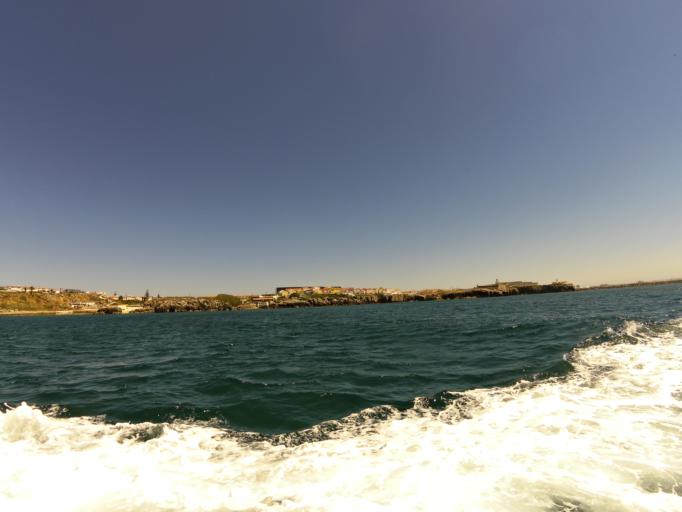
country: PT
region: Leiria
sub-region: Peniche
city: Peniche
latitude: 39.3499
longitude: -9.3883
